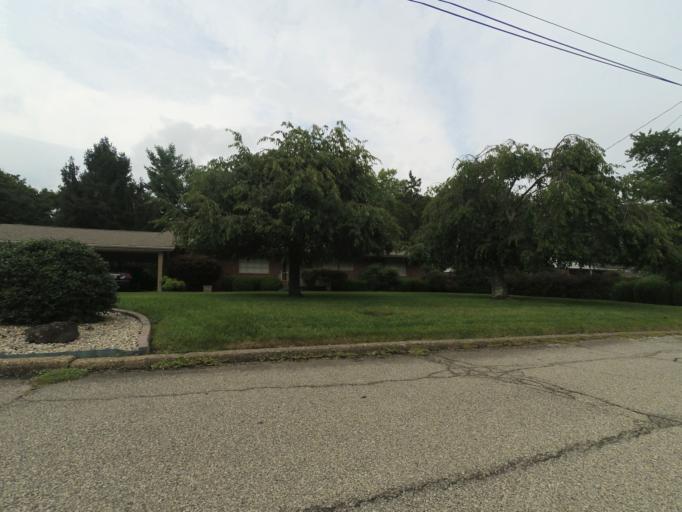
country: US
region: West Virginia
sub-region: Cabell County
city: Huntington
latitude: 38.3968
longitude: -82.4404
